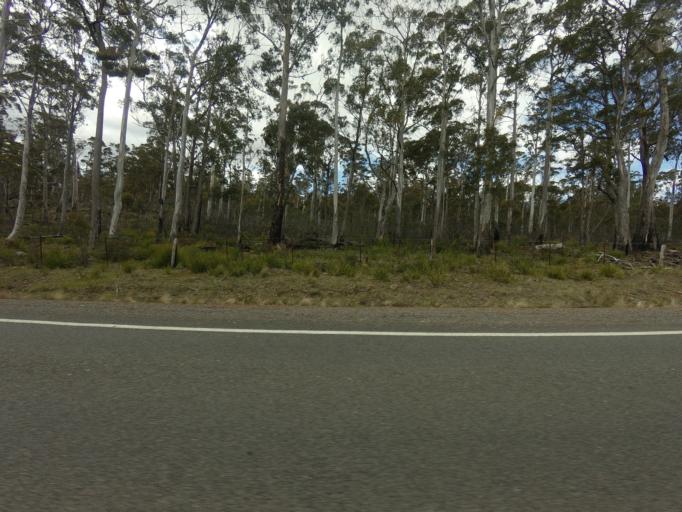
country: AU
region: Tasmania
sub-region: Northern Midlands
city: Evandale
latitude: -41.9942
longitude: 147.7147
